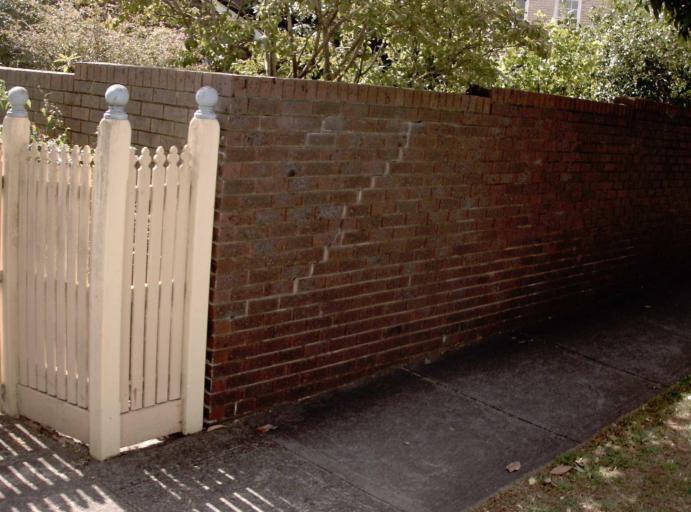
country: AU
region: Victoria
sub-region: Boroondara
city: Hawthorn East
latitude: -37.8131
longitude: 145.0469
